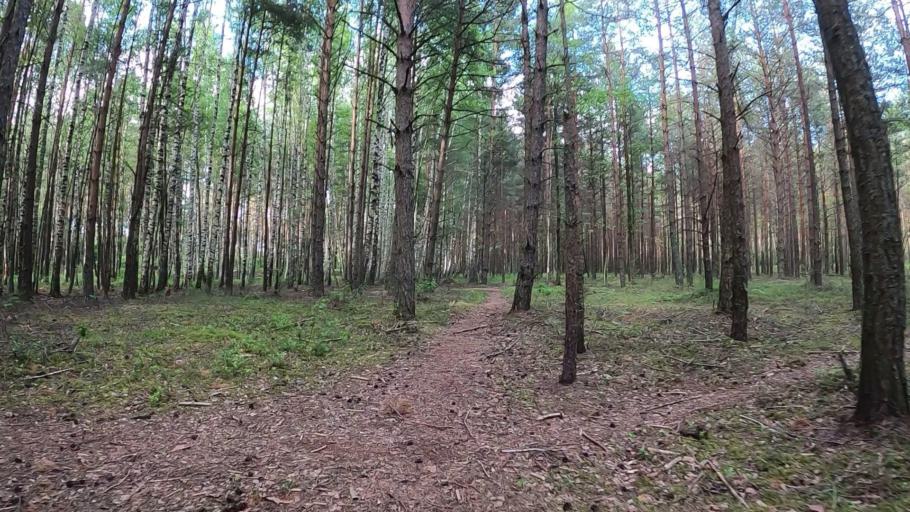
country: LV
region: Riga
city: Jaunciems
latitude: 57.0623
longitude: 24.1306
